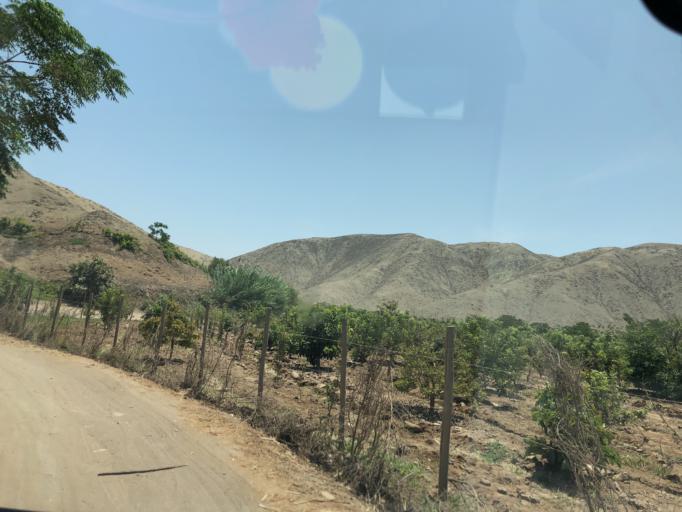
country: PE
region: Lima
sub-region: Provincia de Canete
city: Quilmana
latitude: -12.9976
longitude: -76.4437
